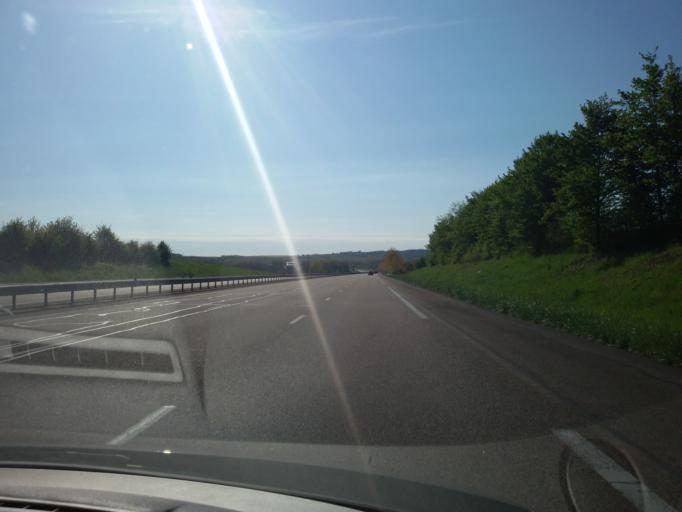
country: FR
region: Bourgogne
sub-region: Departement de l'Yonne
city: Fleury-la-Vallee
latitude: 47.8909
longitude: 3.4104
